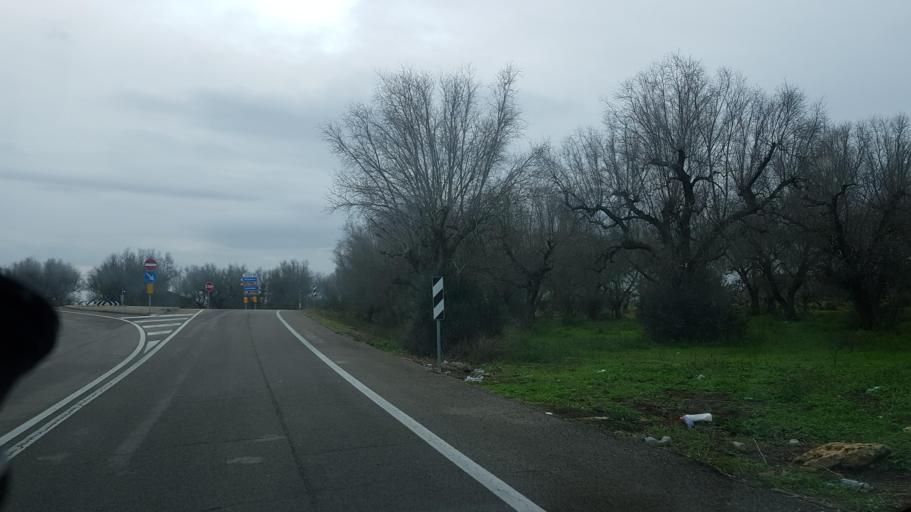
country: IT
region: Apulia
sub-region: Provincia di Brindisi
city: Torchiarolo
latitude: 40.4630
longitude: 18.0563
